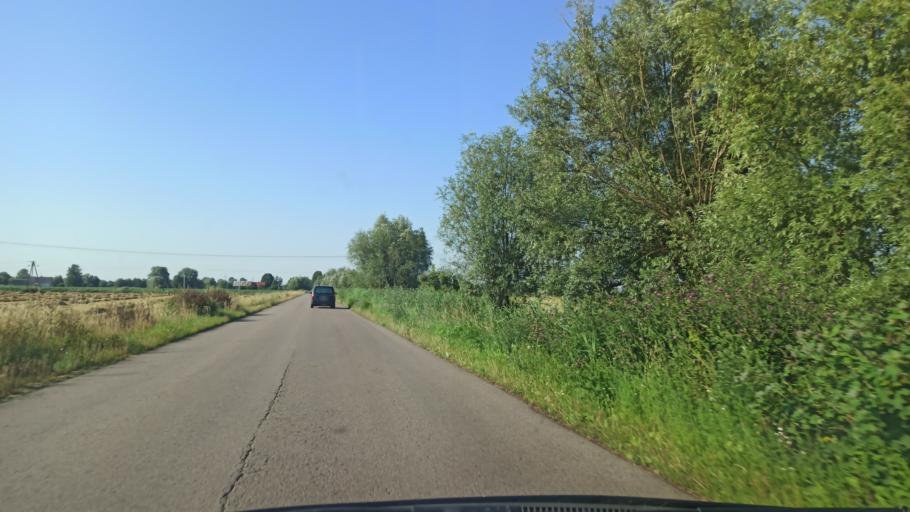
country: PL
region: Warmian-Masurian Voivodeship
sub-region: Powiat elblaski
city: Elblag
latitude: 54.1799
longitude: 19.3321
